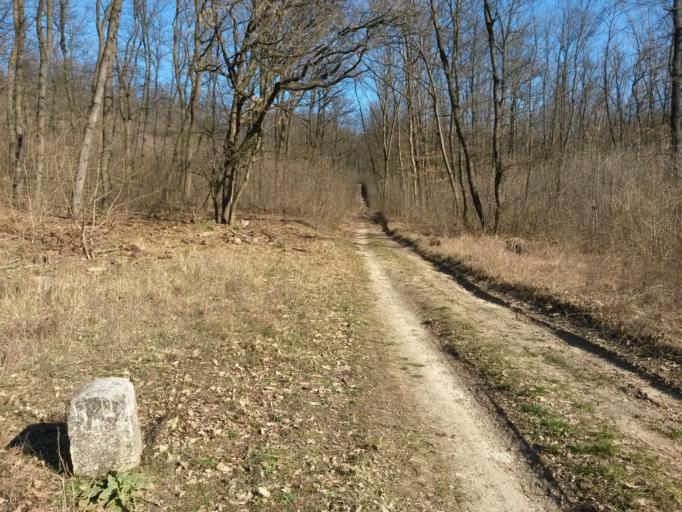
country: HU
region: Pest
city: Piliscsaba
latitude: 47.6008
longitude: 18.8113
